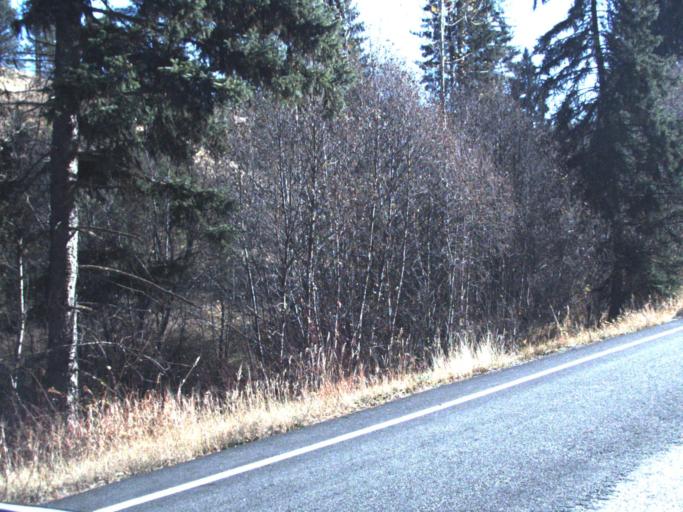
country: US
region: Washington
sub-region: Ferry County
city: Republic
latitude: 48.6225
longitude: -118.6720
